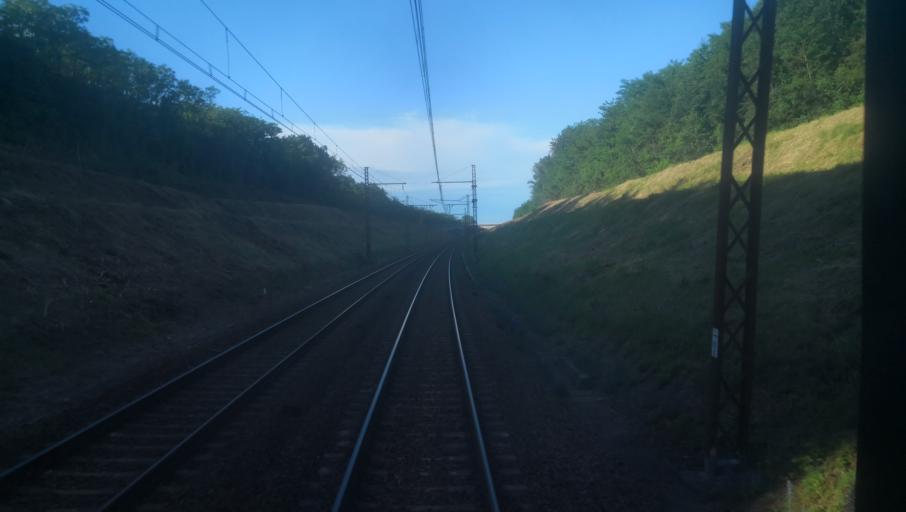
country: FR
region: Centre
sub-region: Departement du Cher
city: Mereau
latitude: 47.1865
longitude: 2.0684
